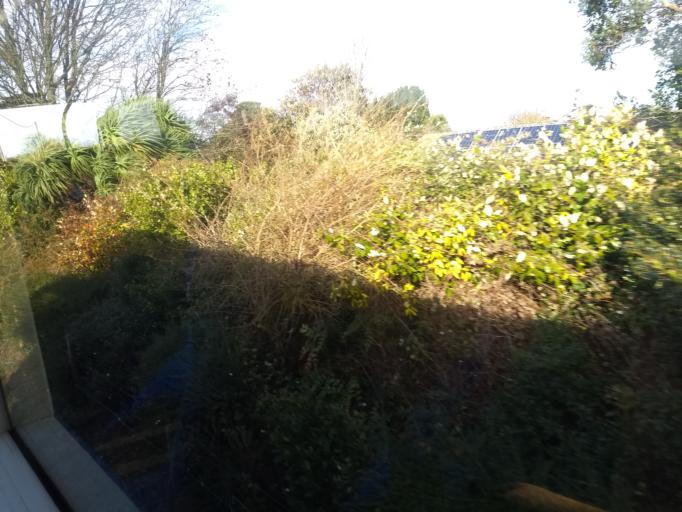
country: GB
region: England
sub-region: Isle of Wight
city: Yarmouth
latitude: 50.6961
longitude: -1.4691
